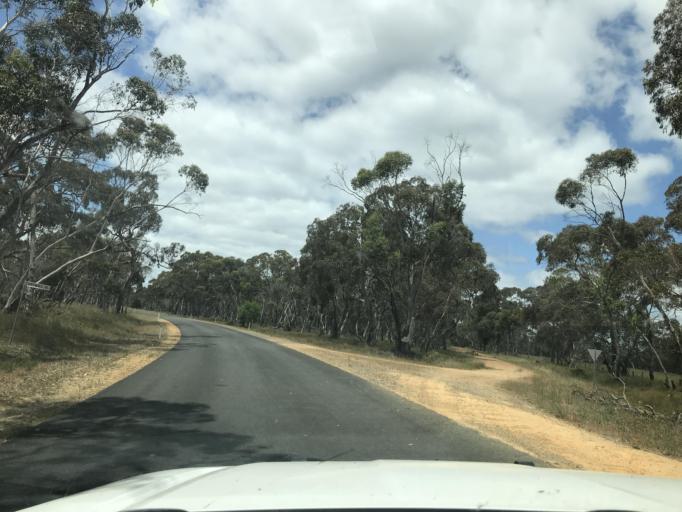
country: AU
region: South Australia
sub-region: Wattle Range
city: Penola
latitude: -37.3577
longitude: 141.1076
